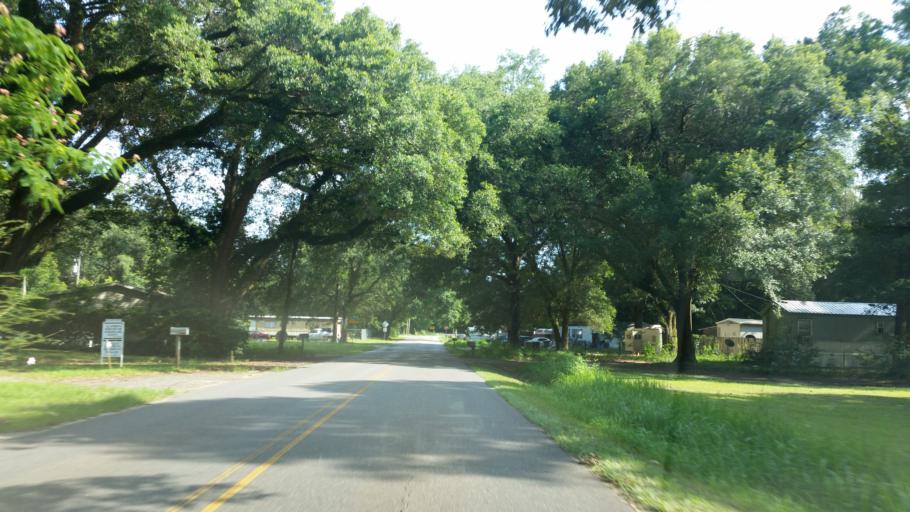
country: US
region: Florida
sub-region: Escambia County
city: Ensley
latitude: 30.5211
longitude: -87.2627
